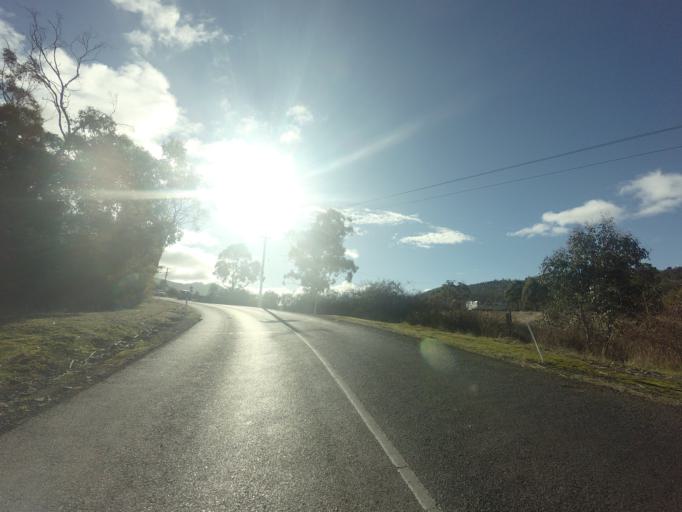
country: AU
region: Tasmania
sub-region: Derwent Valley
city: New Norfolk
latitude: -42.7916
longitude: 147.1230
